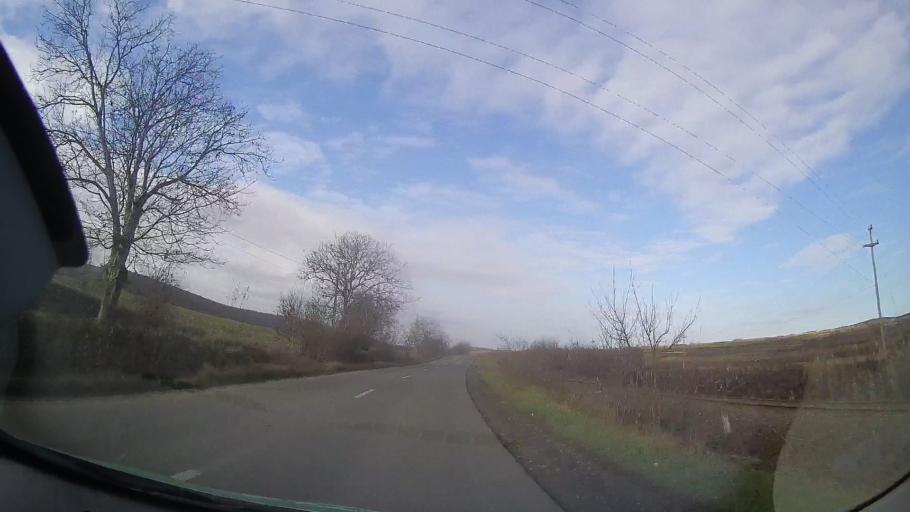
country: RO
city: Barza
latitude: 46.5507
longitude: 24.1151
